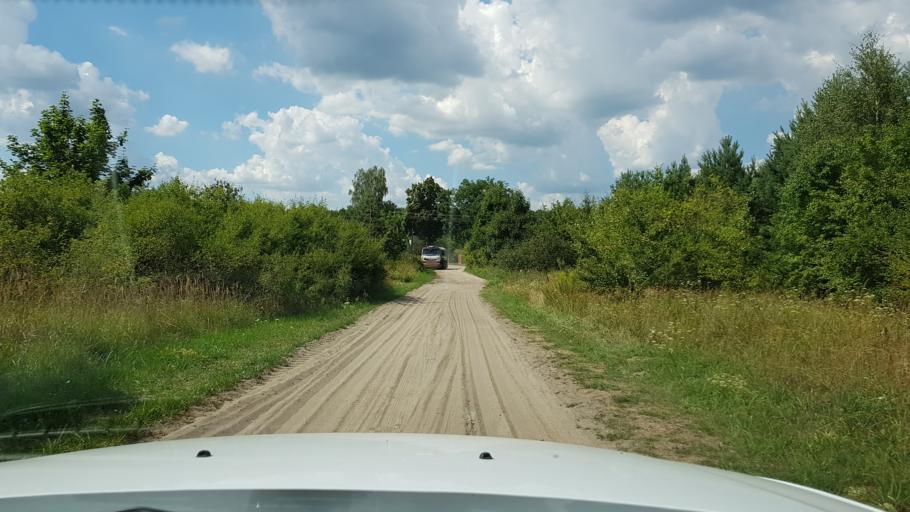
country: PL
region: West Pomeranian Voivodeship
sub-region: Powiat gryfinski
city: Chojna
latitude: 52.9063
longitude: 14.4941
